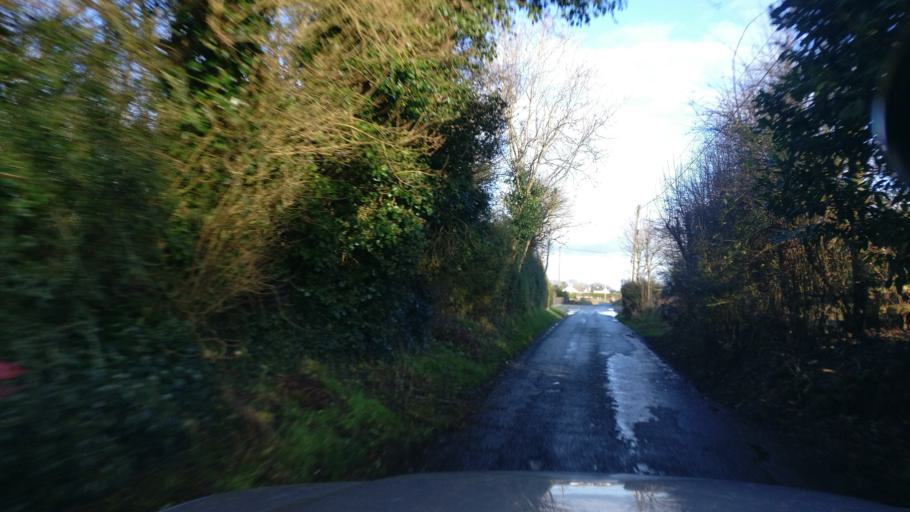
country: IE
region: Connaught
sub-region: County Galway
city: Loughrea
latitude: 53.2263
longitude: -8.5515
